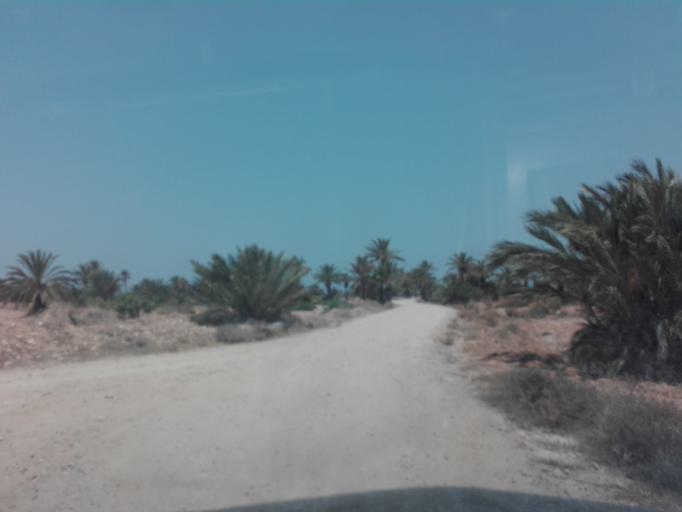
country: TN
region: Safaqis
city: Al Qarmadah
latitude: 34.6629
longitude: 11.0927
